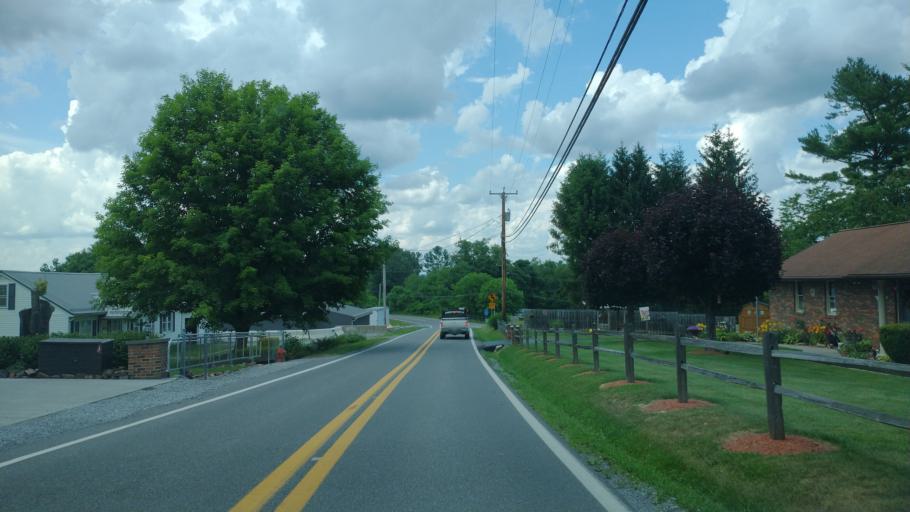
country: US
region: West Virginia
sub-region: Mercer County
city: Athens
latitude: 37.4178
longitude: -81.0630
